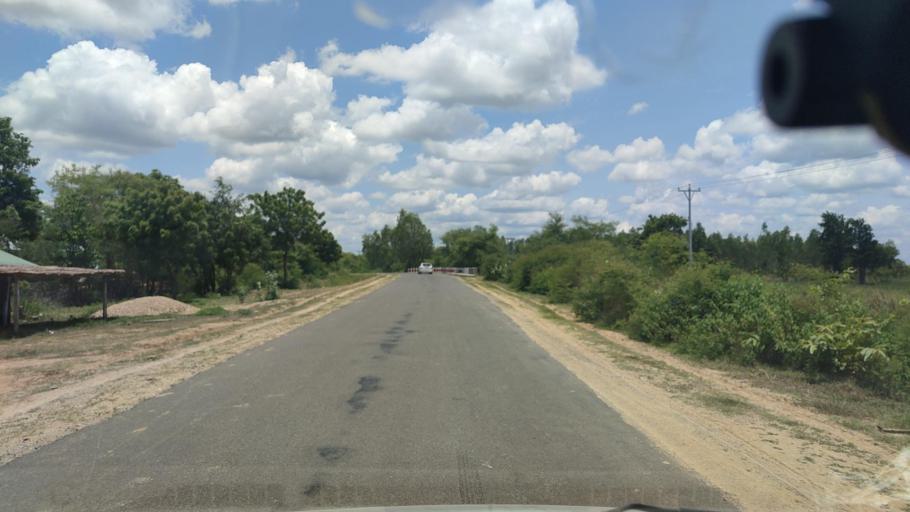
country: MM
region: Magway
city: Taungdwingyi
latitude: 20.1480
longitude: 95.5220
